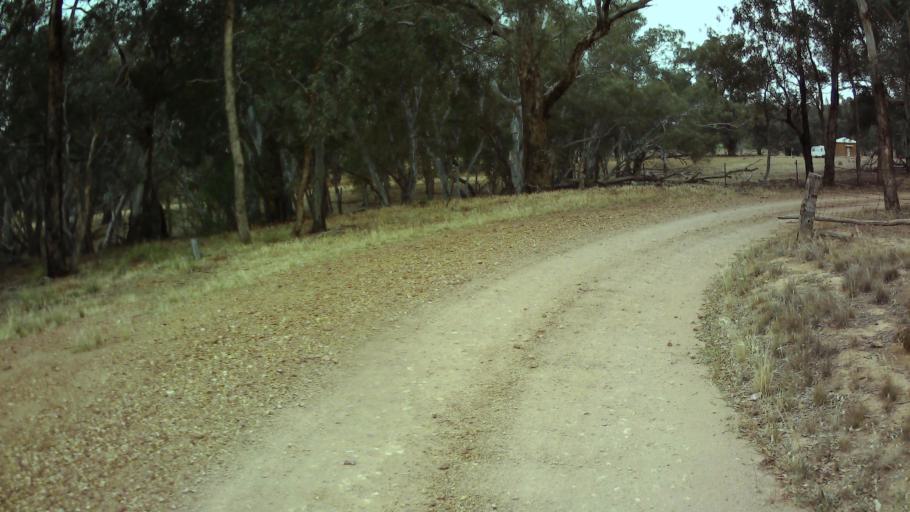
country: AU
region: New South Wales
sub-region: Weddin
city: Grenfell
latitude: -33.9285
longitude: 148.2607
